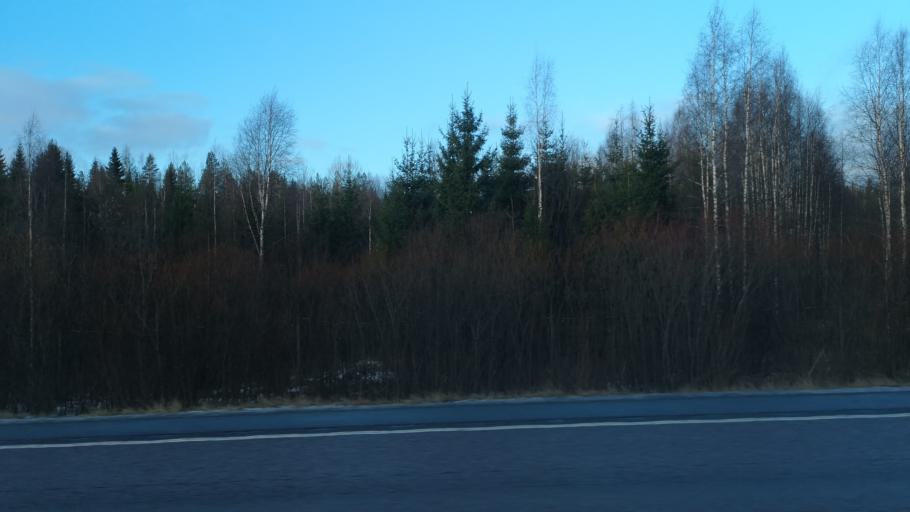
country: FI
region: Paijanne Tavastia
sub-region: Lahti
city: Heinola
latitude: 61.3512
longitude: 26.2193
